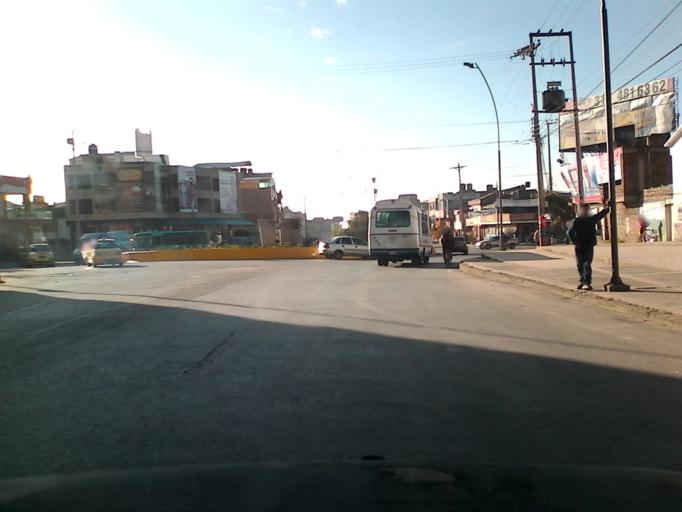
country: CO
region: Boyaca
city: Duitama
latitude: 5.8244
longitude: -73.0274
